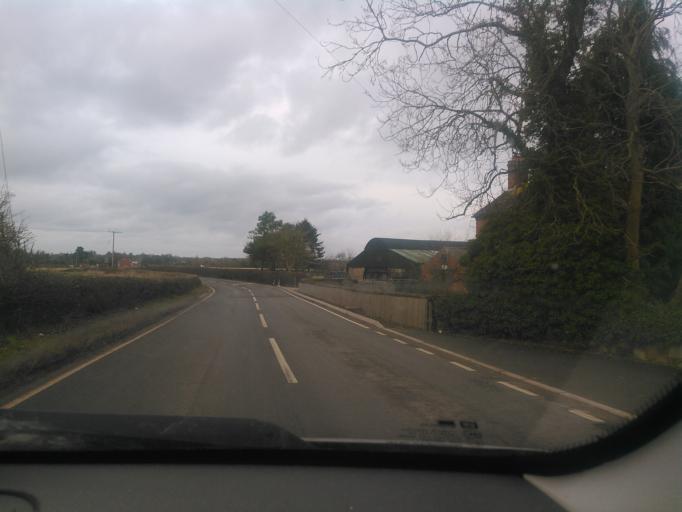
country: GB
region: England
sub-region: Shropshire
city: Wem
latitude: 52.8417
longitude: -2.7111
